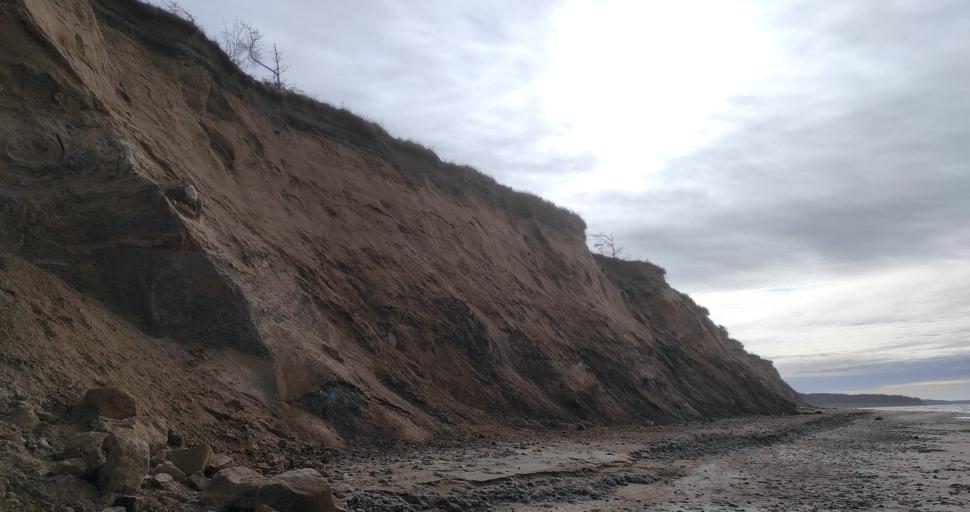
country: LV
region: Alsunga
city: Alsunga
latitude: 57.0420
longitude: 21.4041
